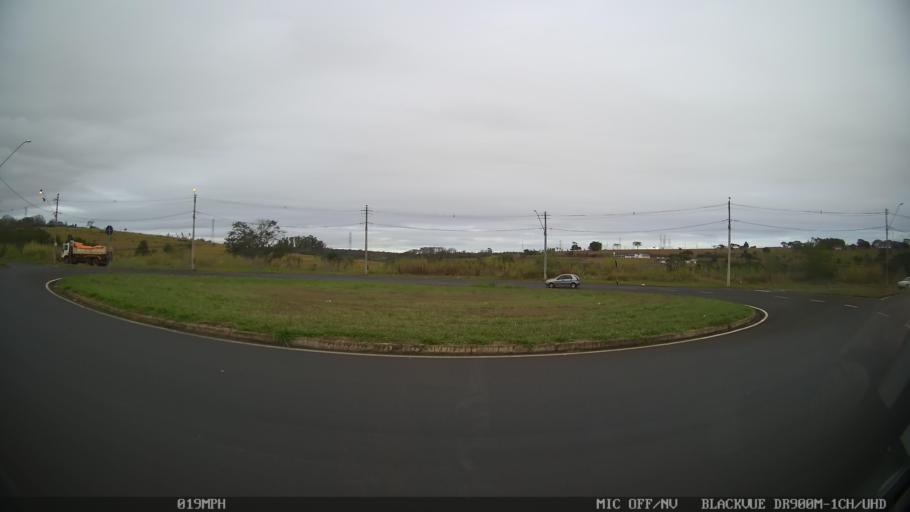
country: BR
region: Sao Paulo
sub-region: Sao Jose Do Rio Preto
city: Sao Jose do Rio Preto
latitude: -20.8227
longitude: -49.4366
